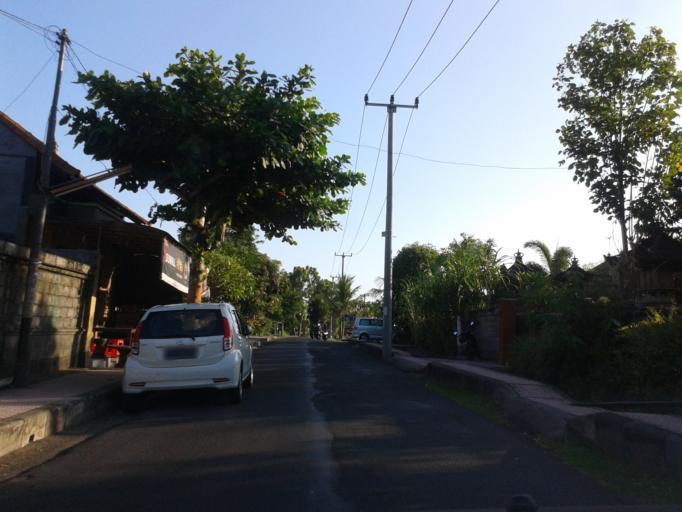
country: ID
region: Bali
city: Klungkung
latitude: -8.5563
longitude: 115.3876
